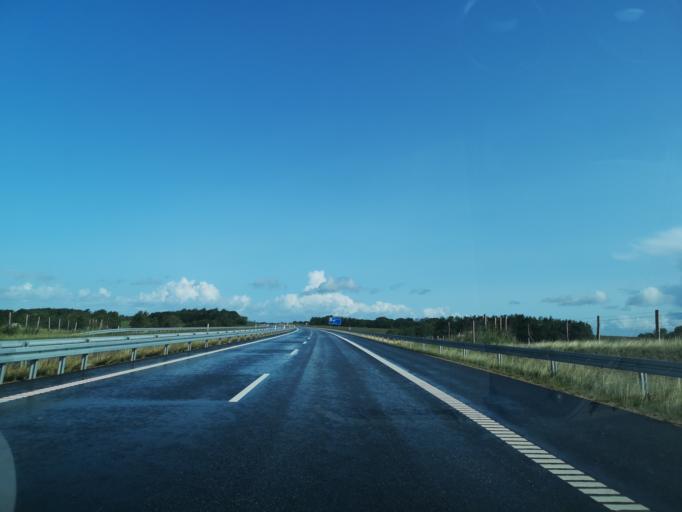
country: DK
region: Central Jutland
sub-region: Herning Kommune
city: Snejbjerg
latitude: 56.1755
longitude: 8.8924
